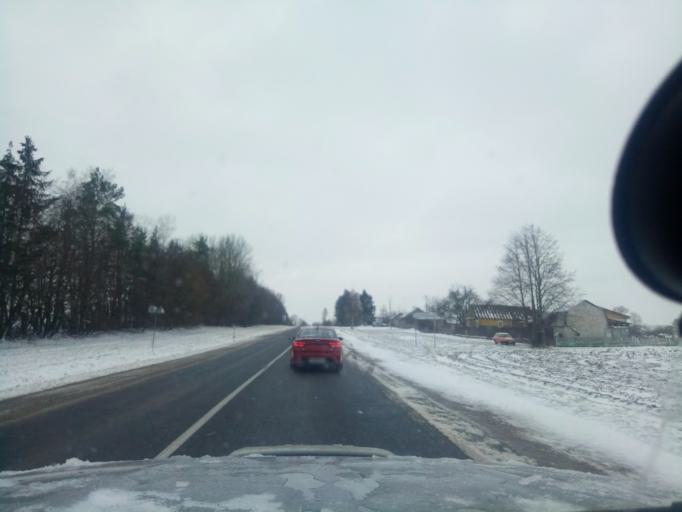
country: BY
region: Minsk
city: Nyasvizh
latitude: 53.1358
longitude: 26.6752
